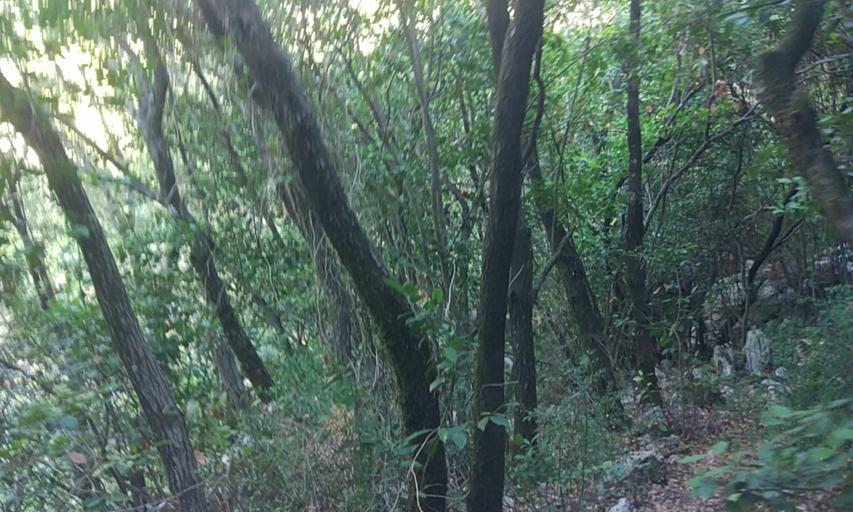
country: TR
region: Antalya
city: Tekirova
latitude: 36.3781
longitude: 30.4782
